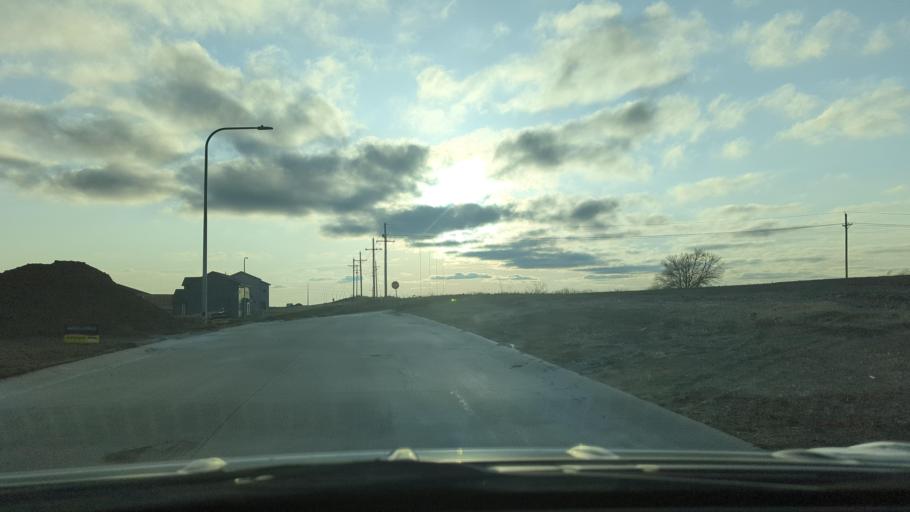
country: US
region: Nebraska
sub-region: Sarpy County
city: Offutt Air Force Base
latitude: 41.1181
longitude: -95.9800
